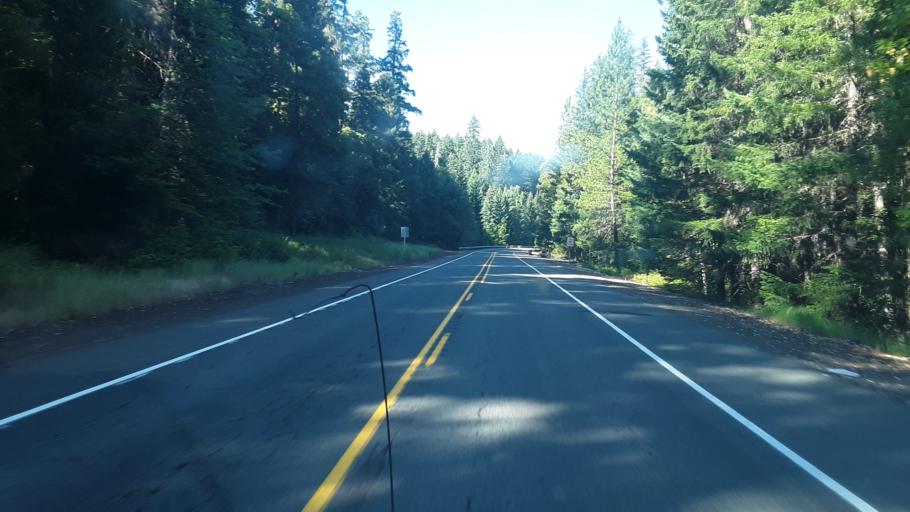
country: US
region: Oregon
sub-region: Jackson County
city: Shady Cove
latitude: 42.6774
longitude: -122.6197
